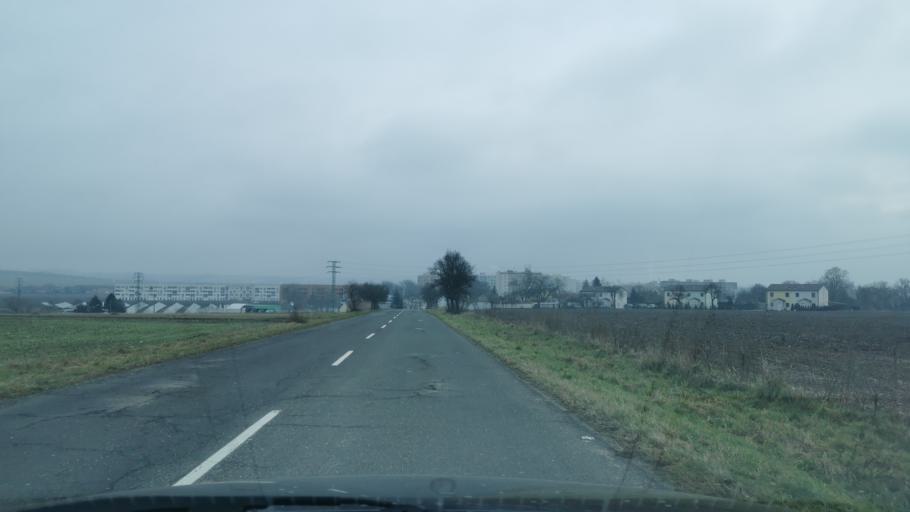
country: SK
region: Trnavsky
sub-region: Okres Senica
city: Senica
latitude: 48.6906
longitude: 17.3616
